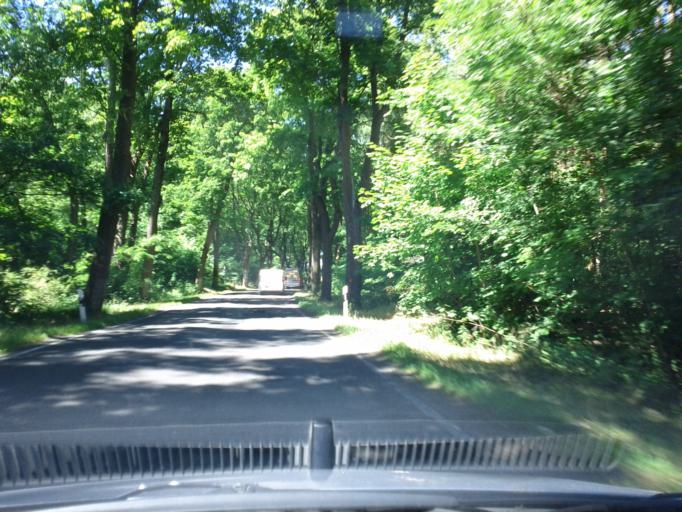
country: DE
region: Brandenburg
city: Rehfelde
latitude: 52.4697
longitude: 13.9542
